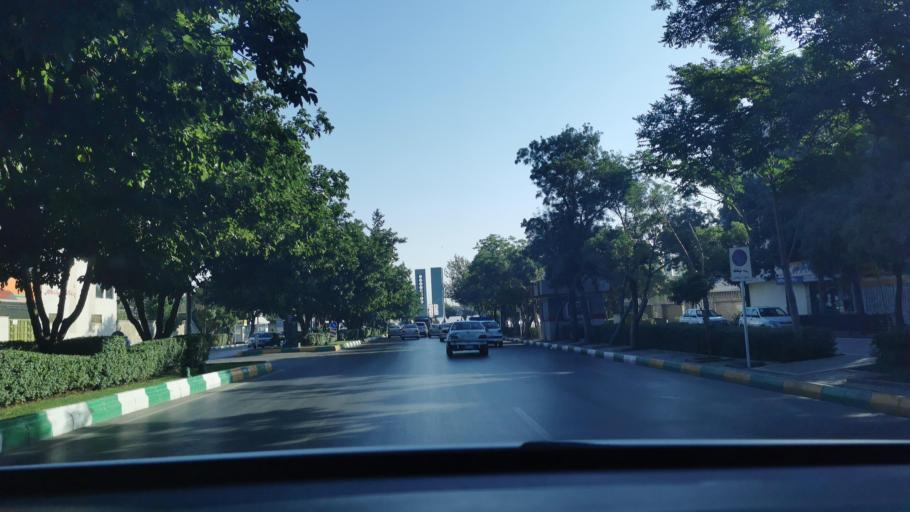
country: IR
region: Razavi Khorasan
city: Mashhad
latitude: 36.2988
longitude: 59.5627
